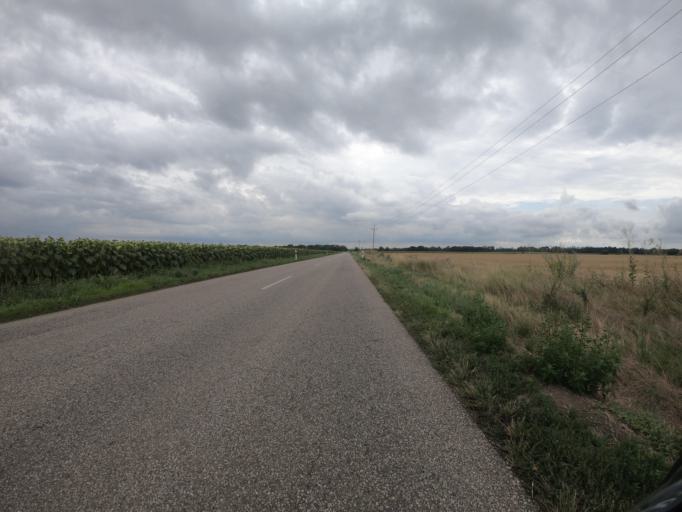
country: HU
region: Borsod-Abauj-Zemplen
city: Mezokovesd
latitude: 47.8016
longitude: 20.5986
